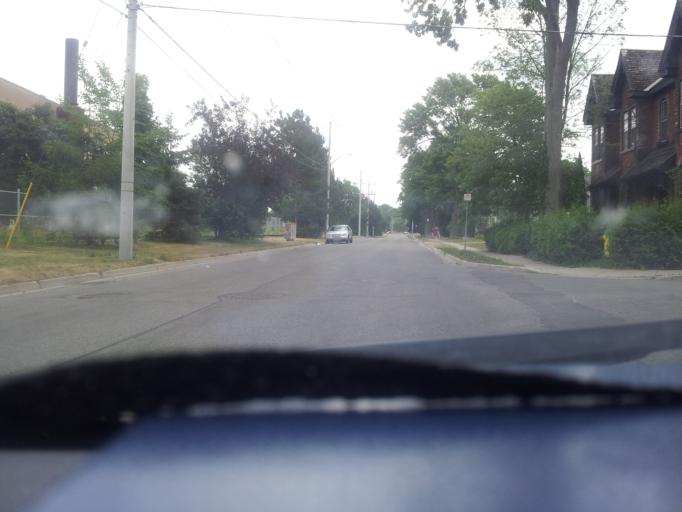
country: CA
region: Ontario
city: Stratford
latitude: 43.3658
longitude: -80.9826
